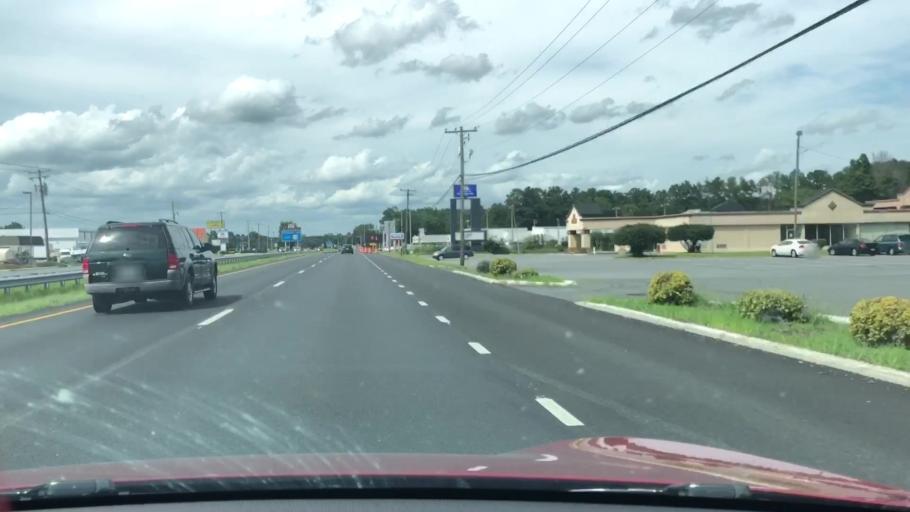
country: US
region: Maryland
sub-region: Worcester County
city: Pocomoke City
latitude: 38.0512
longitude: -75.5433
